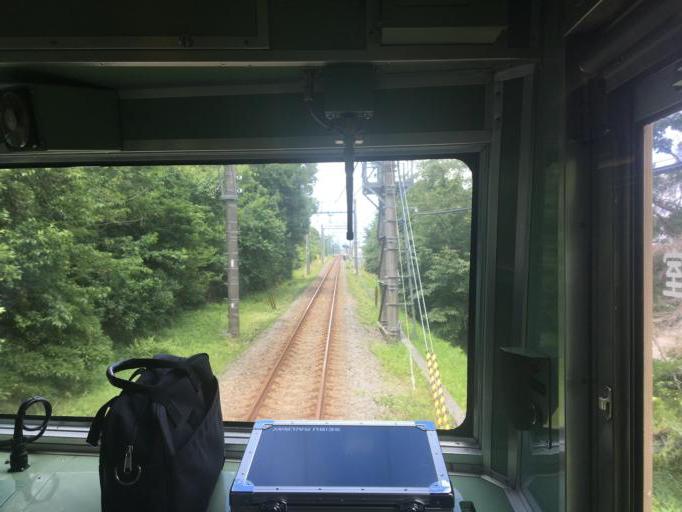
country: JP
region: Tokyo
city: Higashimurayama-shi
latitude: 35.7439
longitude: 139.4701
